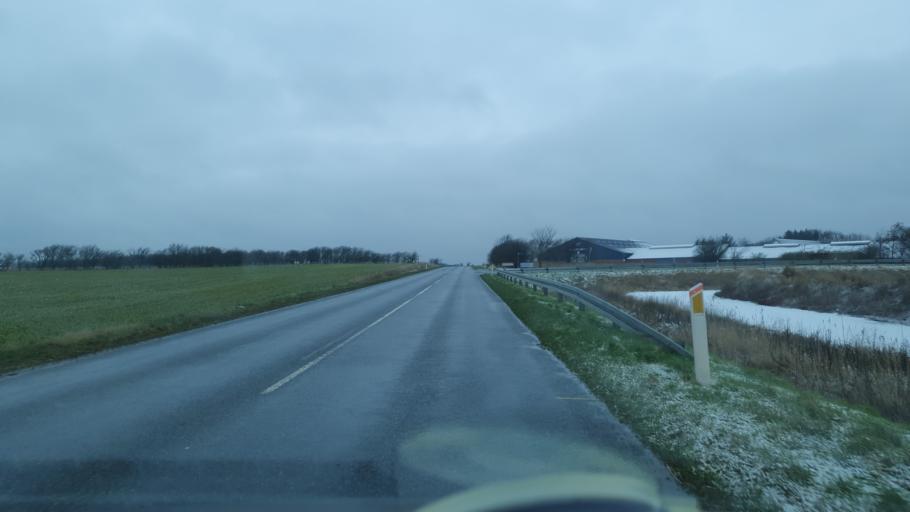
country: DK
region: North Denmark
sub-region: Jammerbugt Kommune
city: Brovst
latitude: 57.1220
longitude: 9.4926
